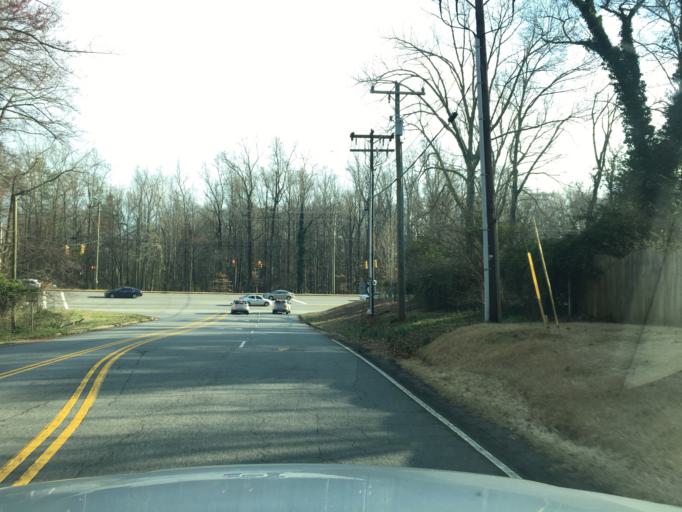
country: US
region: South Carolina
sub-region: Greenville County
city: Wade Hampton
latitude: 34.8603
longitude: -82.2942
